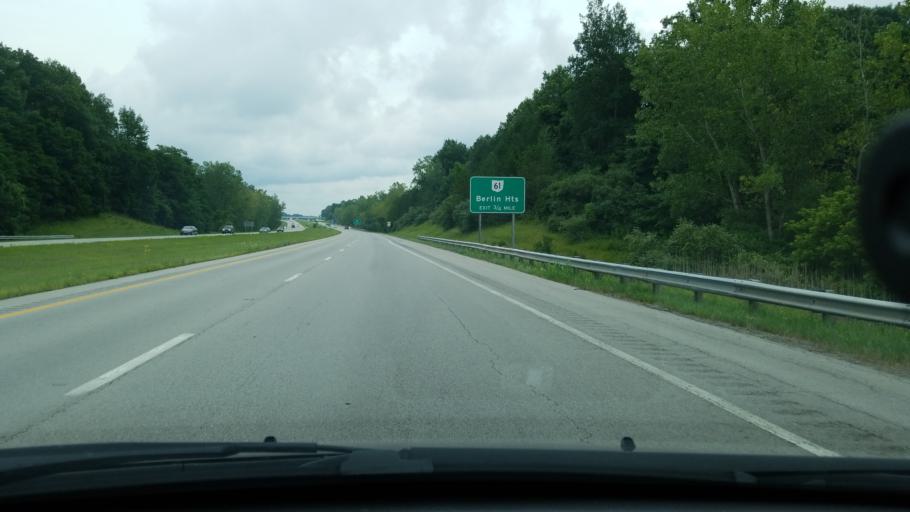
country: US
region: Ohio
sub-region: Erie County
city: Huron
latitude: 41.3670
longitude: -82.5124
